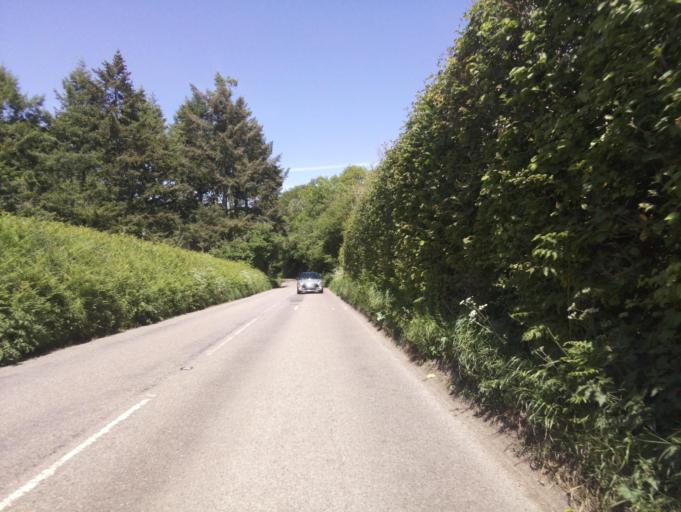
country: GB
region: England
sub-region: Devon
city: Newton Poppleford
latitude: 50.7079
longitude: -3.2685
